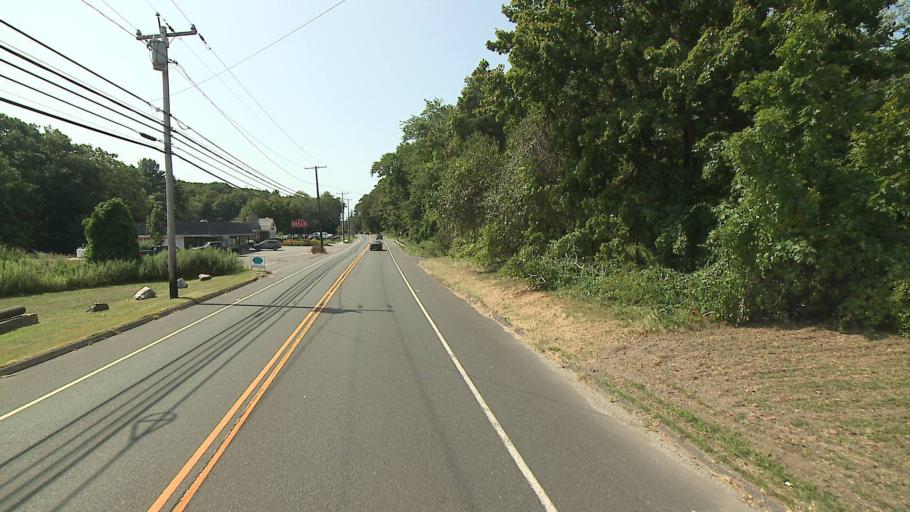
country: US
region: Connecticut
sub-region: Fairfield County
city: Newtown
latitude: 41.3317
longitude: -73.2650
